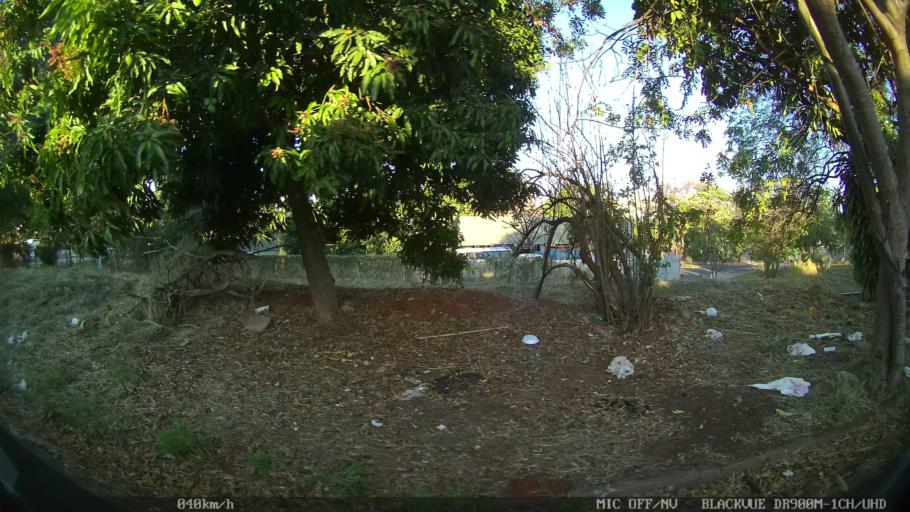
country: BR
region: Sao Paulo
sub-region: Sao Jose Do Rio Preto
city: Sao Jose do Rio Preto
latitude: -20.7999
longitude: -49.3791
